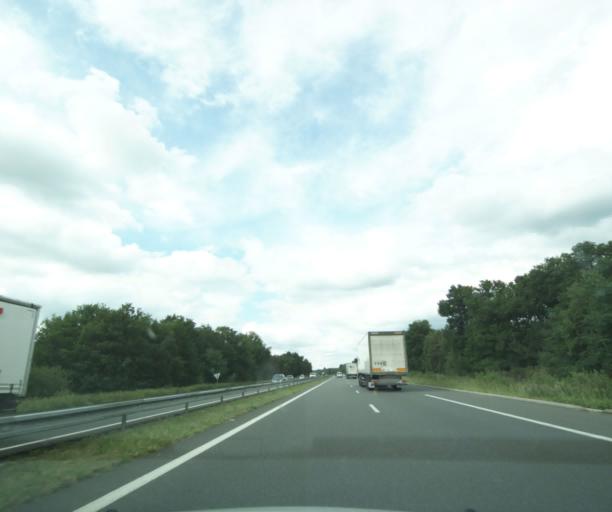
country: FR
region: Centre
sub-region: Departement du Loir-et-Cher
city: Salbris
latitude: 47.4664
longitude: 2.0068
